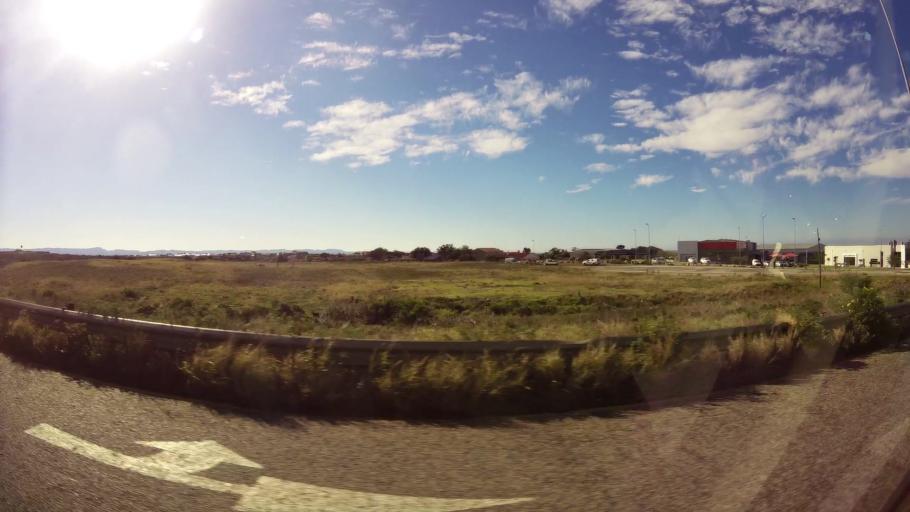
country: ZA
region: Eastern Cape
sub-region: Cacadu District Municipality
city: Jeffrey's Bay
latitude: -34.0289
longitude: 24.9001
